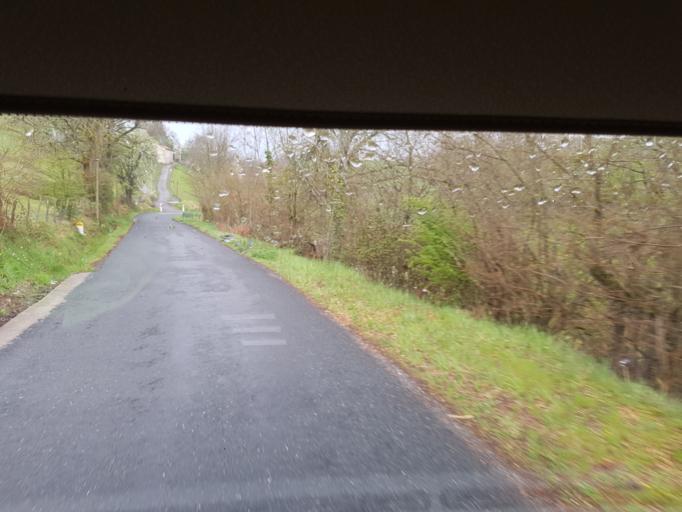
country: FR
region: Rhone-Alpes
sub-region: Departement de la Loire
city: Le Chambon-Feugerolles
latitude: 45.4030
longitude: 4.3267
